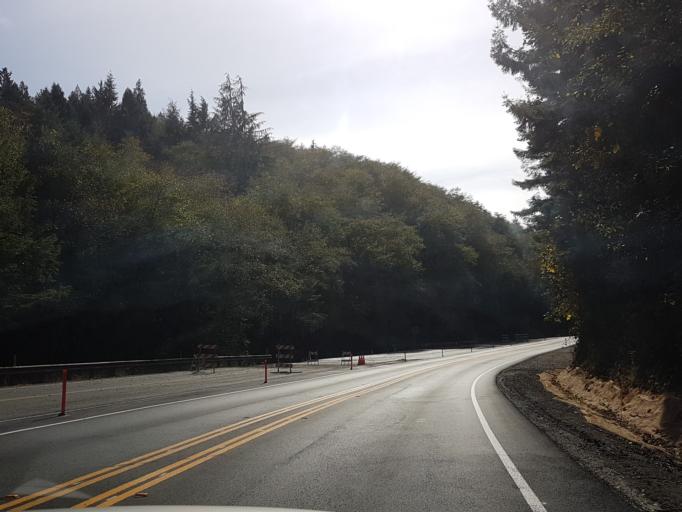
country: US
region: California
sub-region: Del Norte County
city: Bertsch-Oceanview
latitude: 41.4939
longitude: -124.0443
